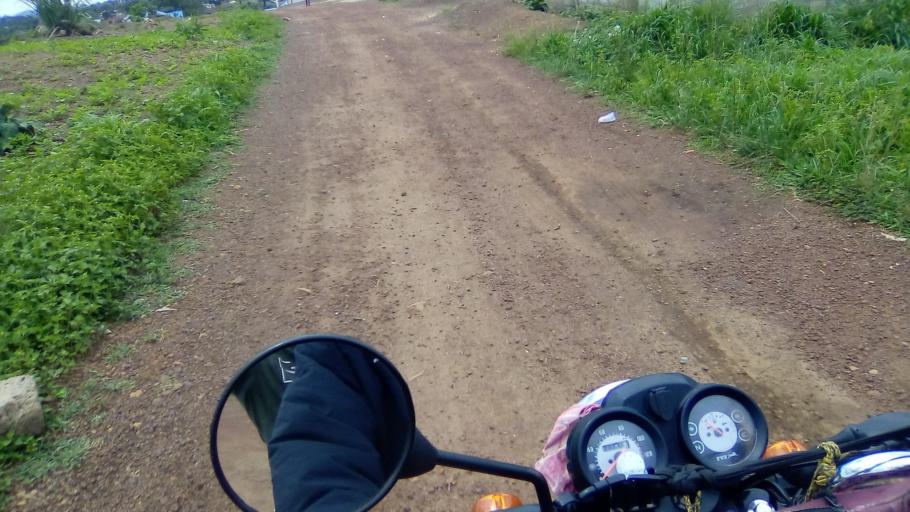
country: SL
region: Southern Province
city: Bo
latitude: 7.9348
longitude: -11.7202
